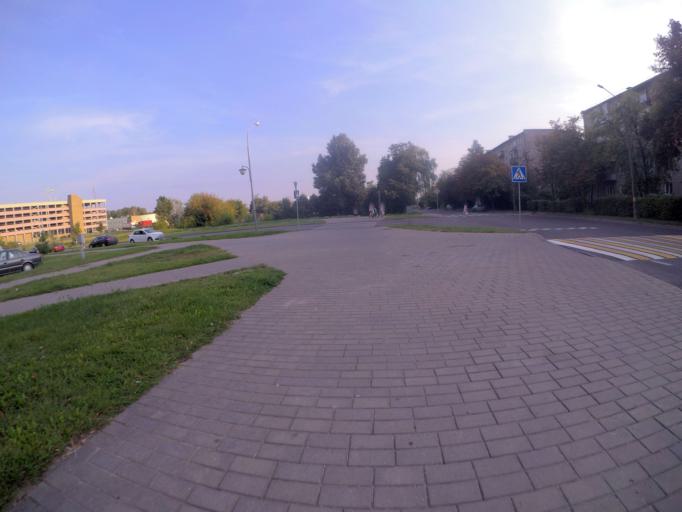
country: BY
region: Grodnenskaya
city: Hrodna
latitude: 53.6947
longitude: 23.8352
